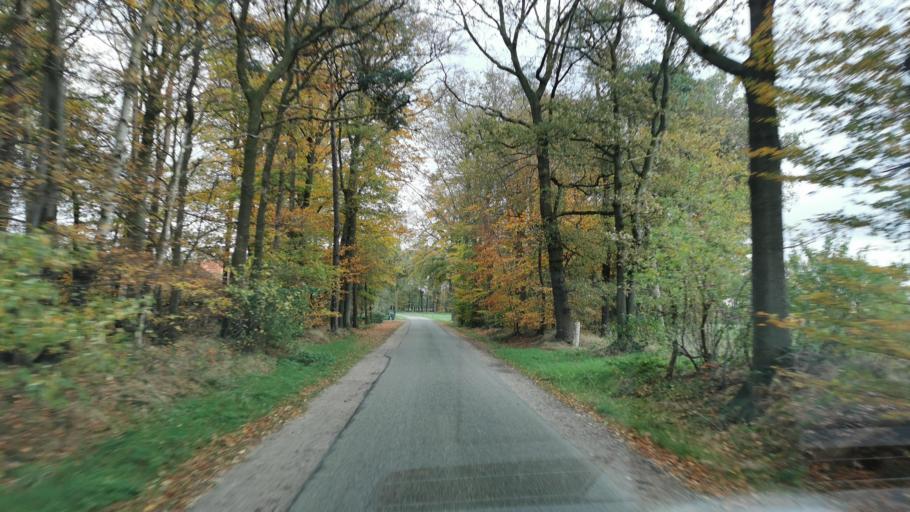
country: NL
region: Overijssel
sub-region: Gemeente Losser
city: Losser
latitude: 52.2474
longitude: 7.0406
